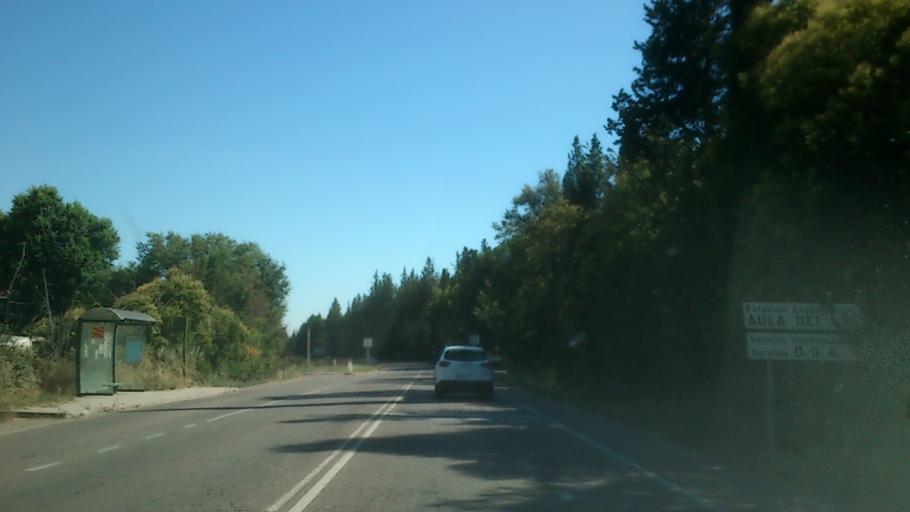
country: ES
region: Aragon
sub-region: Provincia de Zaragoza
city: Villanueva de Gallego
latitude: 41.7249
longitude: -0.8104
